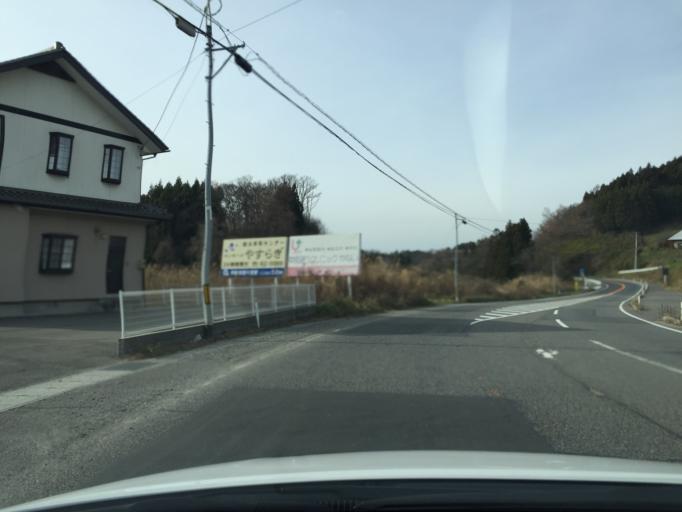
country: JP
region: Fukushima
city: Funehikimachi-funehiki
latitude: 37.4363
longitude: 140.5515
